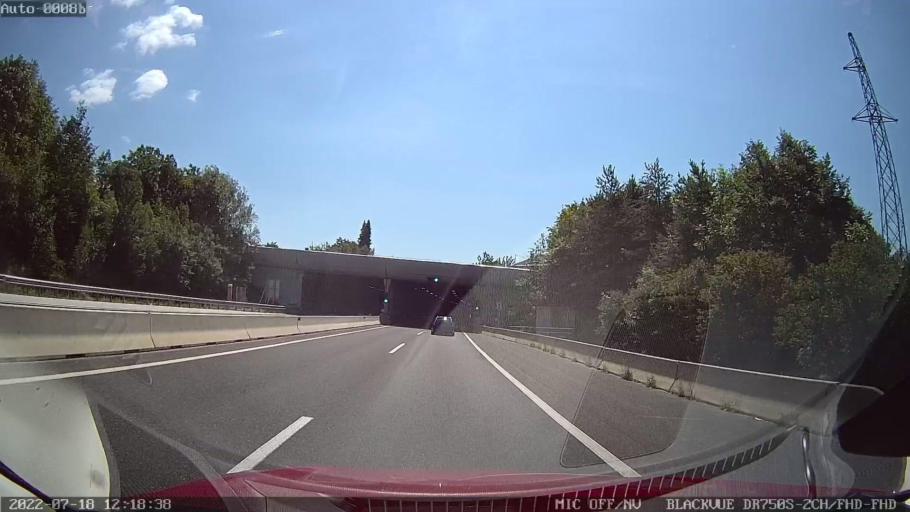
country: SI
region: Zirovnica
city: Zirovnica
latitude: 46.4056
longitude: 14.1250
